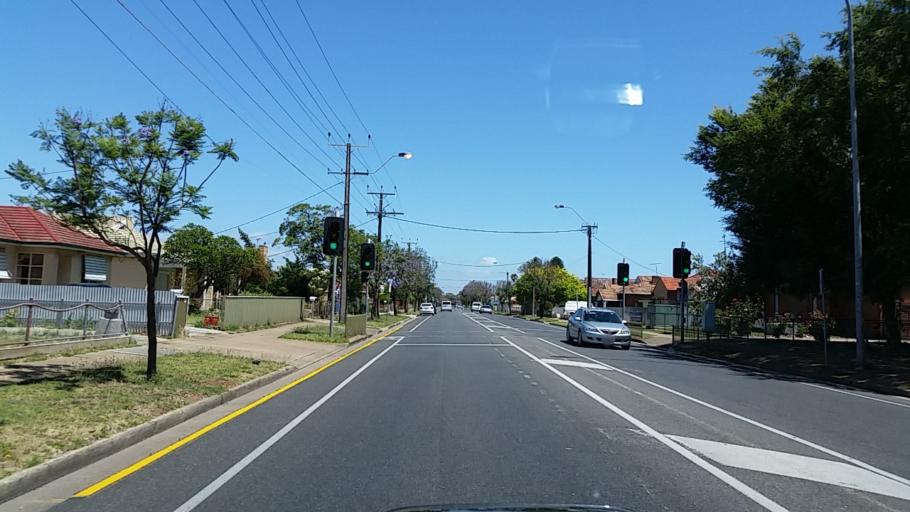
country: AU
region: South Australia
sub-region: Charles Sturt
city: Allenby Gardens
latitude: -34.8994
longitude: 138.5517
